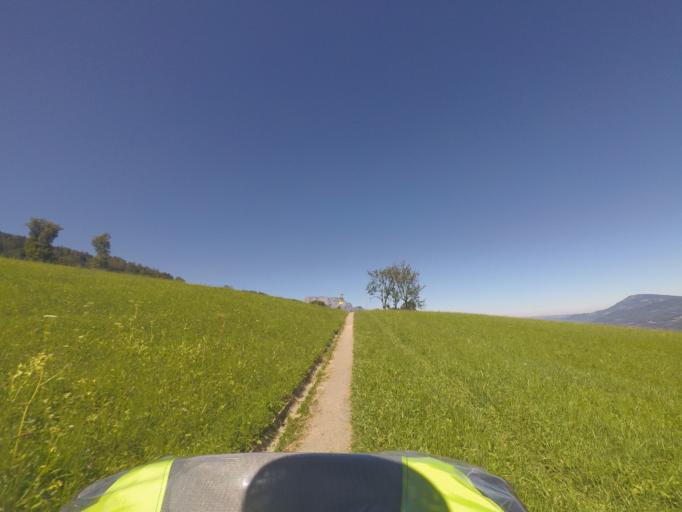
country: AT
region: Salzburg
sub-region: Politischer Bezirk Hallein
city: Hallein
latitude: 47.6583
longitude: 13.0908
